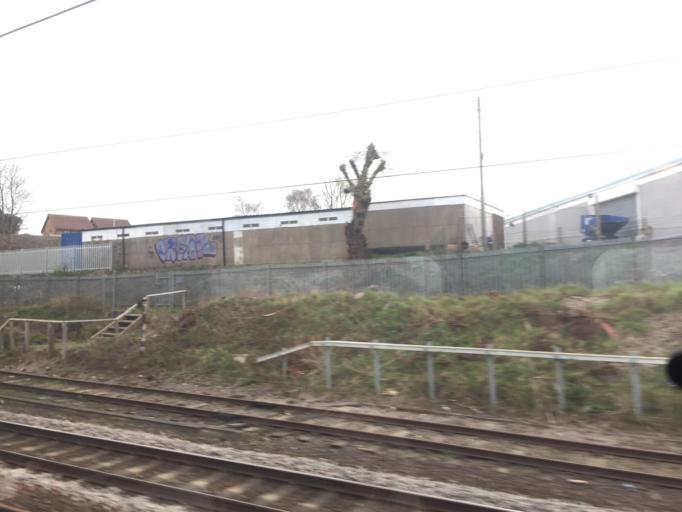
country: GB
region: England
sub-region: Warrington
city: Warrington
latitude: 53.3920
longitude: -2.6038
